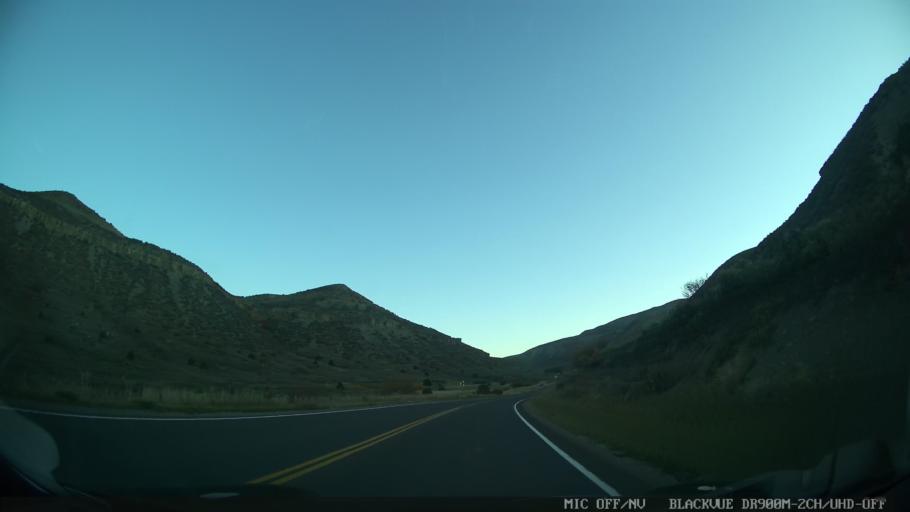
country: US
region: Colorado
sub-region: Eagle County
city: Edwards
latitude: 39.7741
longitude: -106.6834
